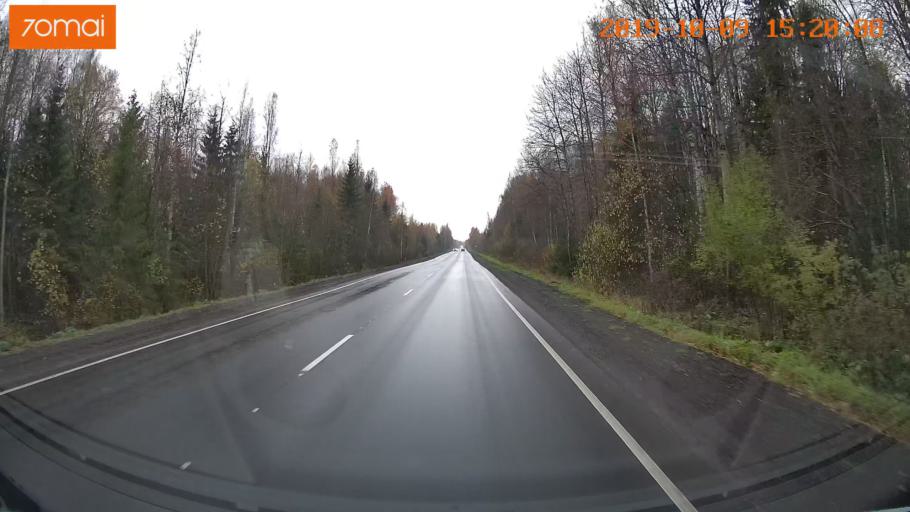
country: RU
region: Kostroma
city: Susanino
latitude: 58.0679
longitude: 41.5435
